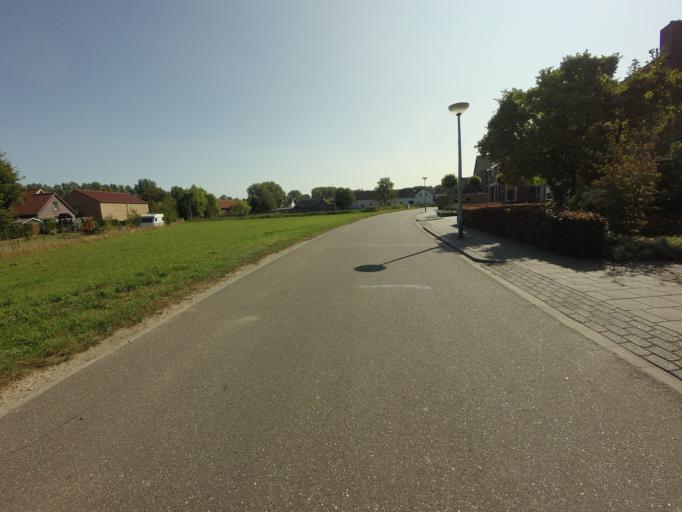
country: NL
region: Limburg
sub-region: Gemeente Roerdalen
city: Vlodrop
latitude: 51.1345
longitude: 6.0786
